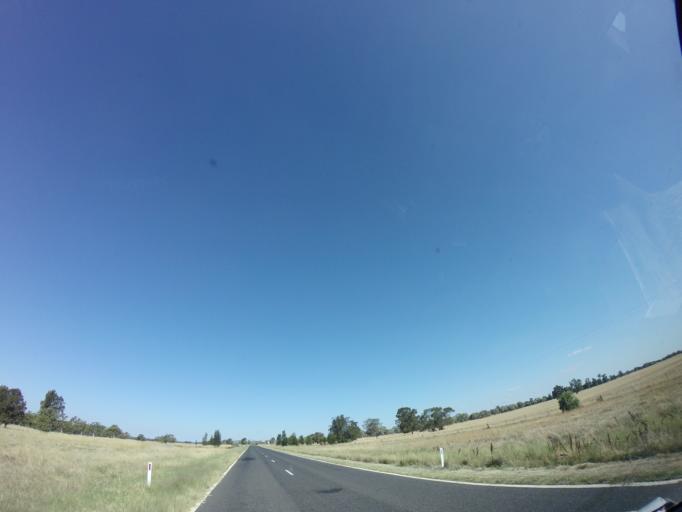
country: AU
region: New South Wales
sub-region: Gilgandra
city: Gilgandra
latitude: -31.6684
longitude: 148.2040
